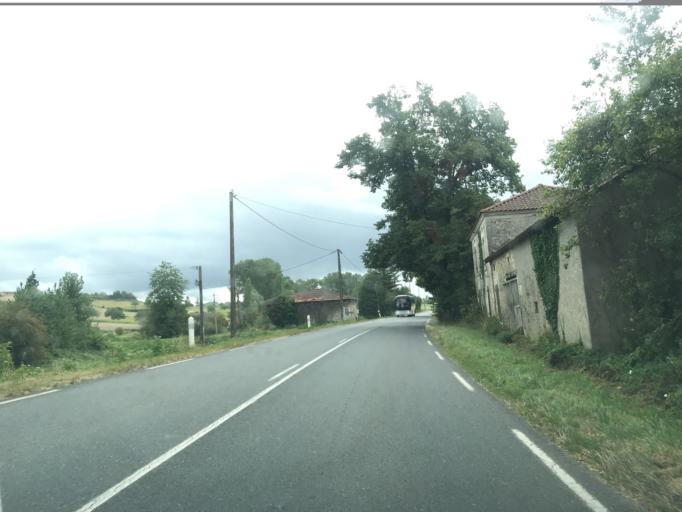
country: FR
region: Aquitaine
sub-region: Departement de la Dordogne
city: Brantome
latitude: 45.4038
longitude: 0.6011
